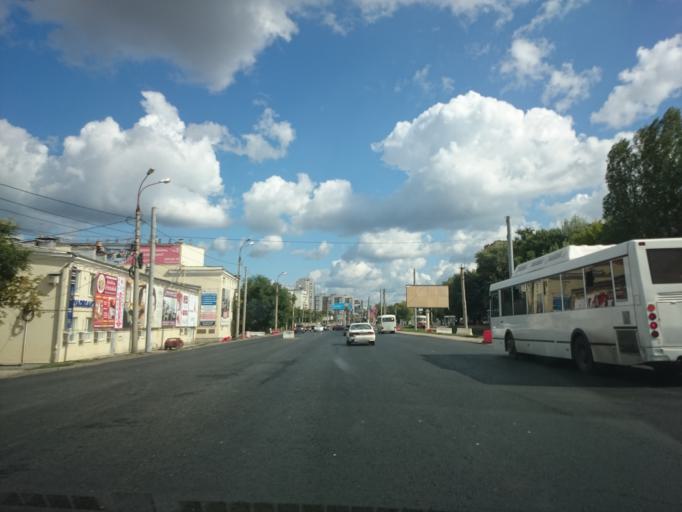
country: RU
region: Samara
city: Samara
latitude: 53.2329
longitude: 50.1840
